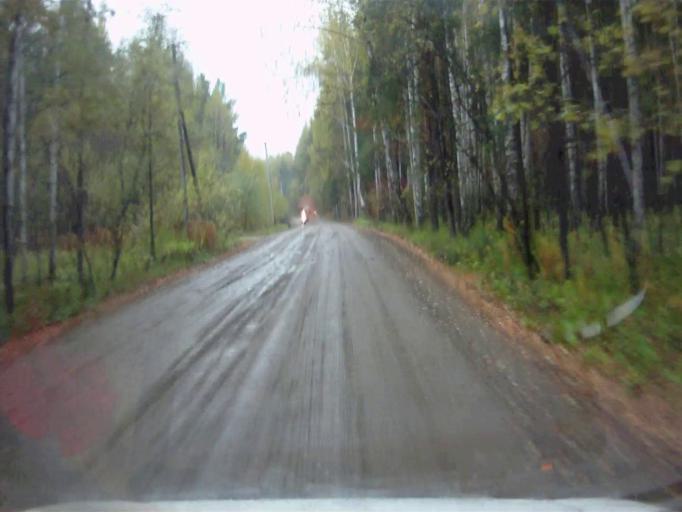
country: RU
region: Chelyabinsk
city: Kyshtym
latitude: 55.8948
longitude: 60.4649
